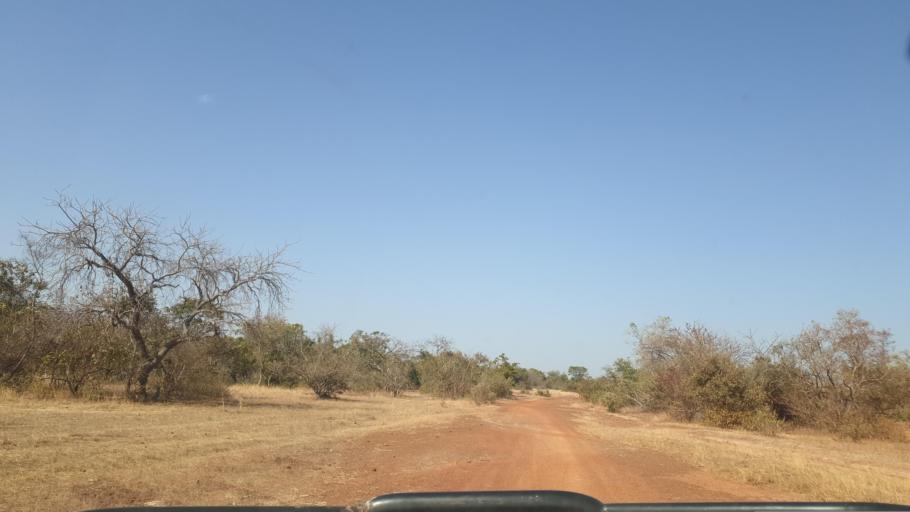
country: ML
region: Sikasso
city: Bougouni
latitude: 11.8191
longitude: -6.9470
